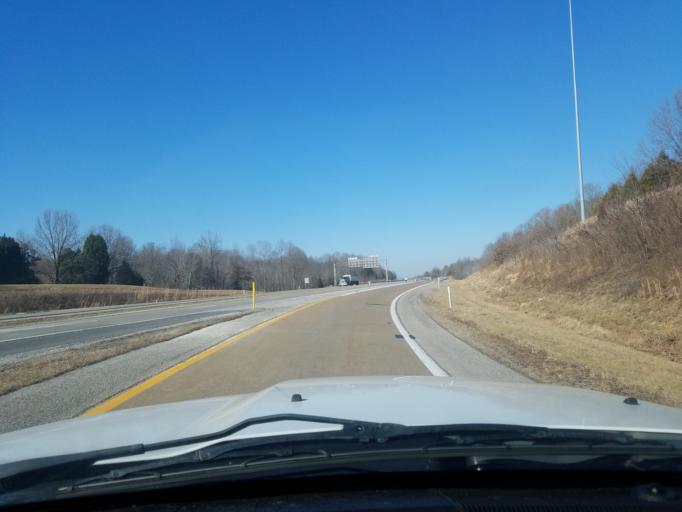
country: US
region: Kentucky
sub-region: Ohio County
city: Beaver Dam
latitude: 37.3879
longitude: -86.8107
